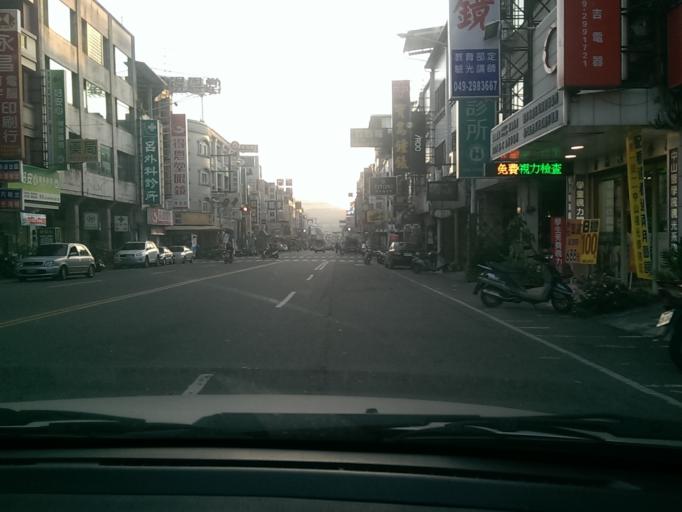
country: TW
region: Taiwan
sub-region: Nantou
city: Puli
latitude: 23.9649
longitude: 120.9670
